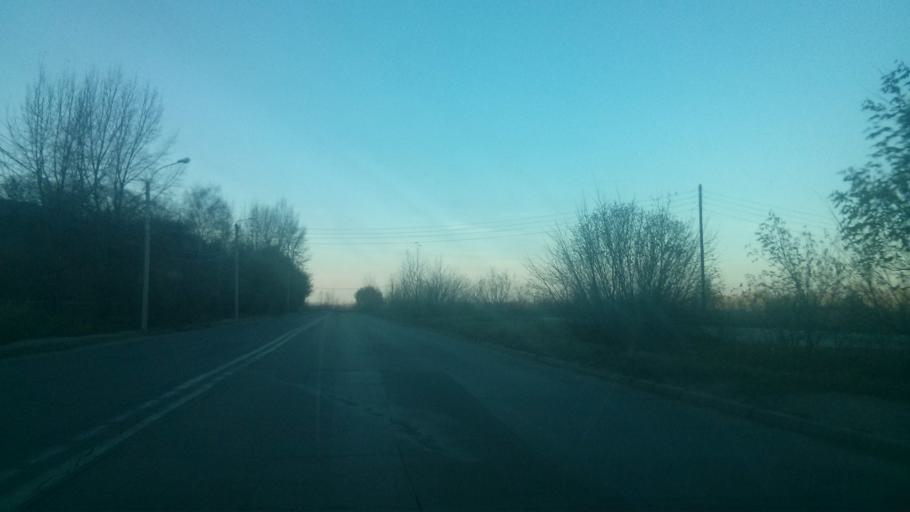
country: RU
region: Nizjnij Novgorod
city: Bor
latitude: 56.3122
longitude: 44.0887
